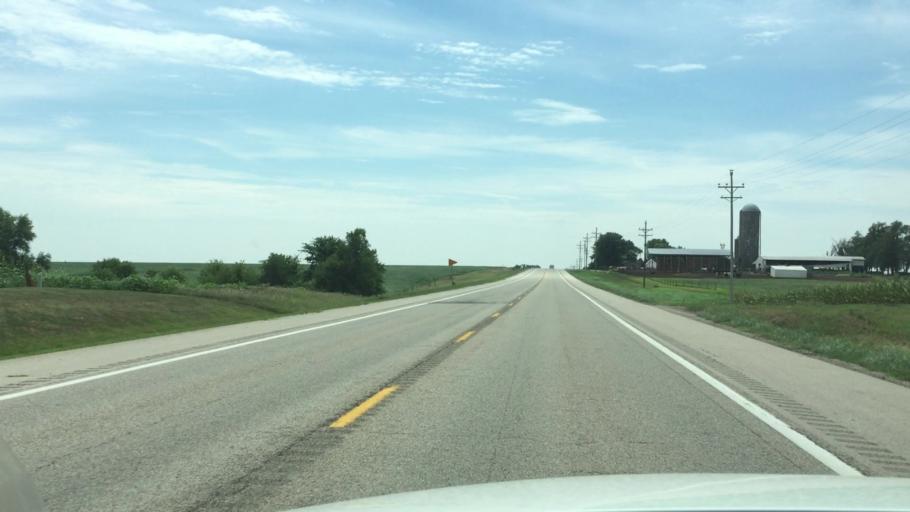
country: US
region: Kansas
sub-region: Nemaha County
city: Sabetha
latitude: 39.7763
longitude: -95.7296
